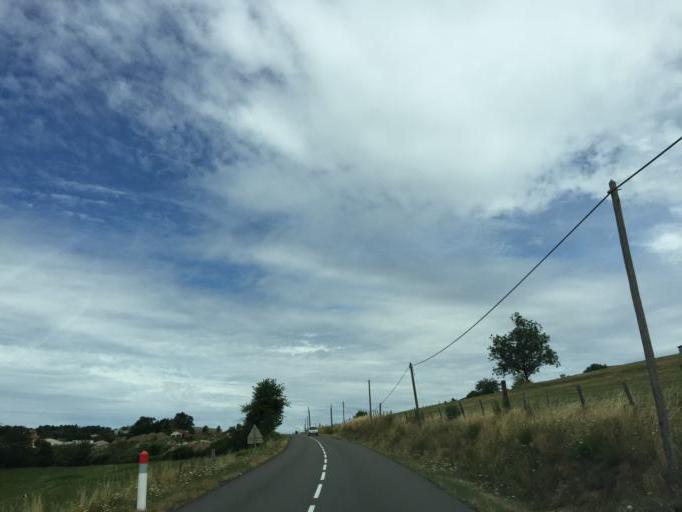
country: FR
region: Rhone-Alpes
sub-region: Departement de la Loire
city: Saint-Bonnet-le-Chateau
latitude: 45.4104
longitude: 4.0959
